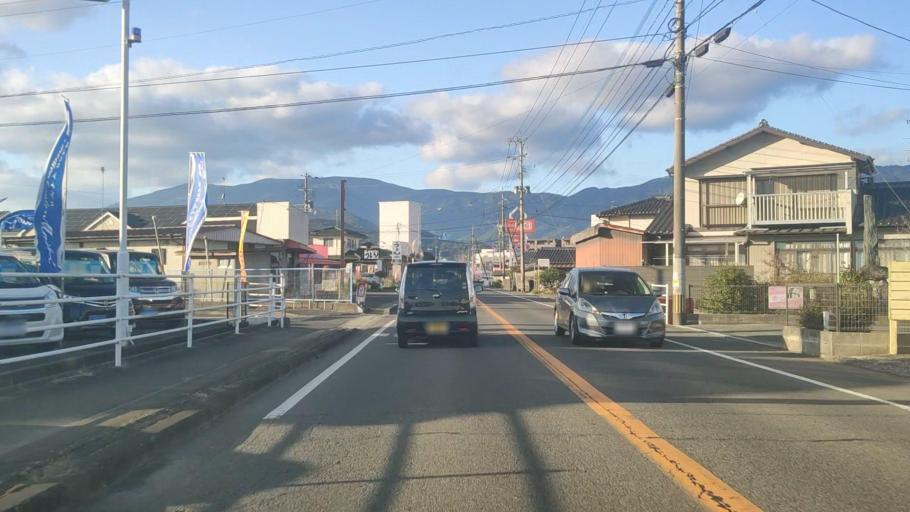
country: JP
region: Saga Prefecture
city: Saga-shi
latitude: 33.2859
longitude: 130.2082
